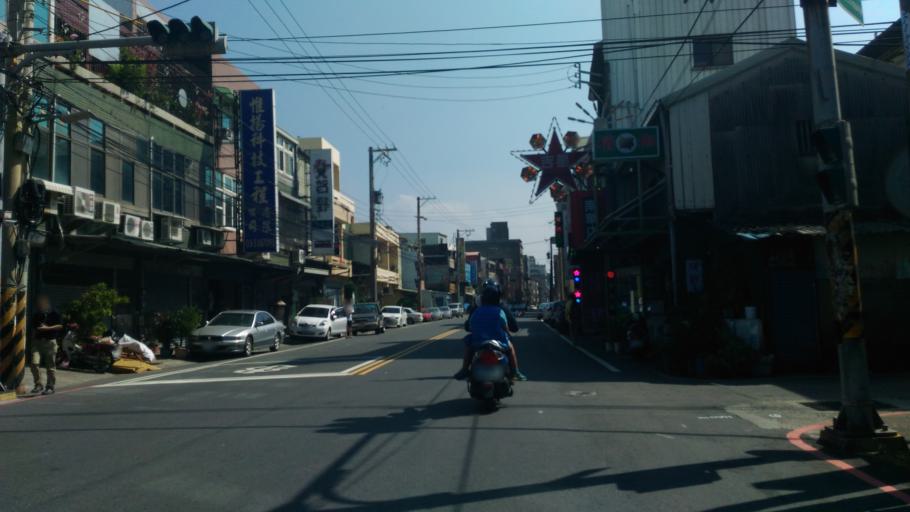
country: TW
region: Taiwan
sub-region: Hsinchu
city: Hsinchu
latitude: 24.8382
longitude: 120.9410
